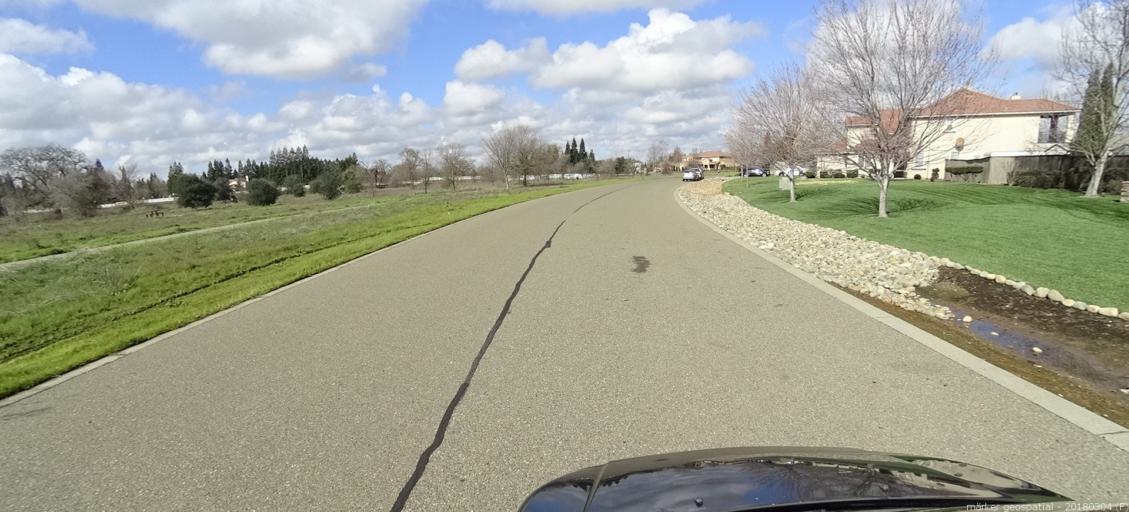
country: US
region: California
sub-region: Sacramento County
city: Vineyard
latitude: 38.4632
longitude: -121.3134
